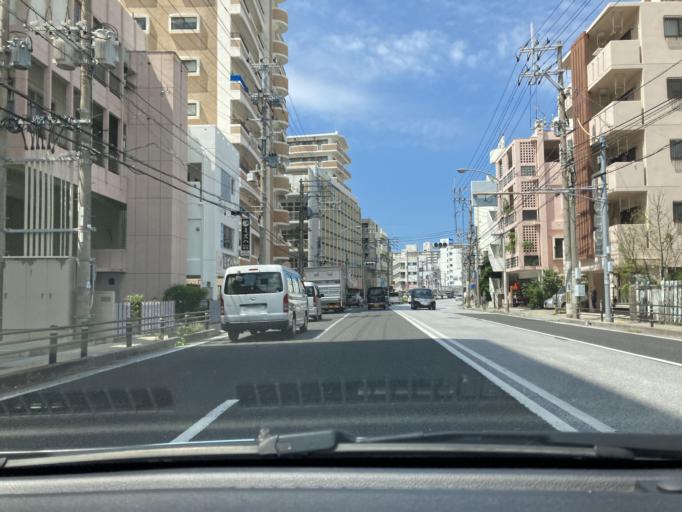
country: JP
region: Okinawa
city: Naha-shi
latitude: 26.2034
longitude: 127.6830
